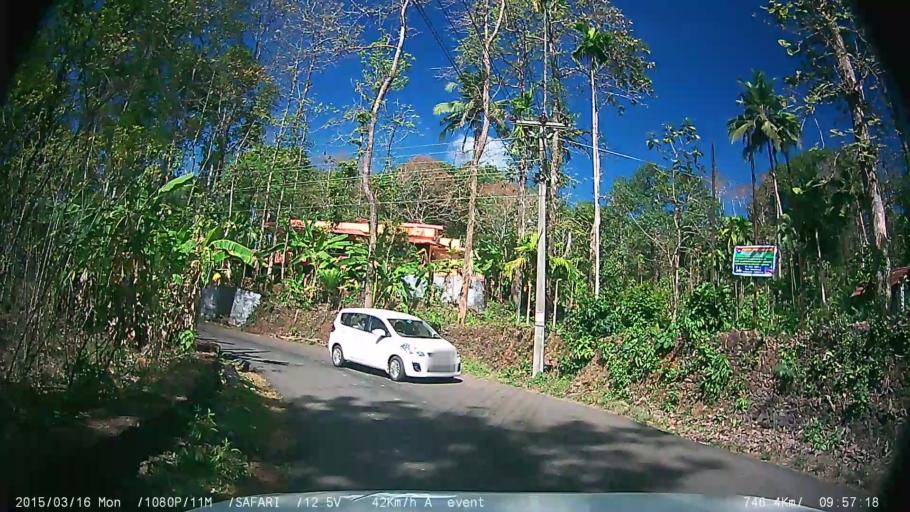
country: IN
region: Kerala
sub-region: Kottayam
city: Palackattumala
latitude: 9.7884
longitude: 76.6058
